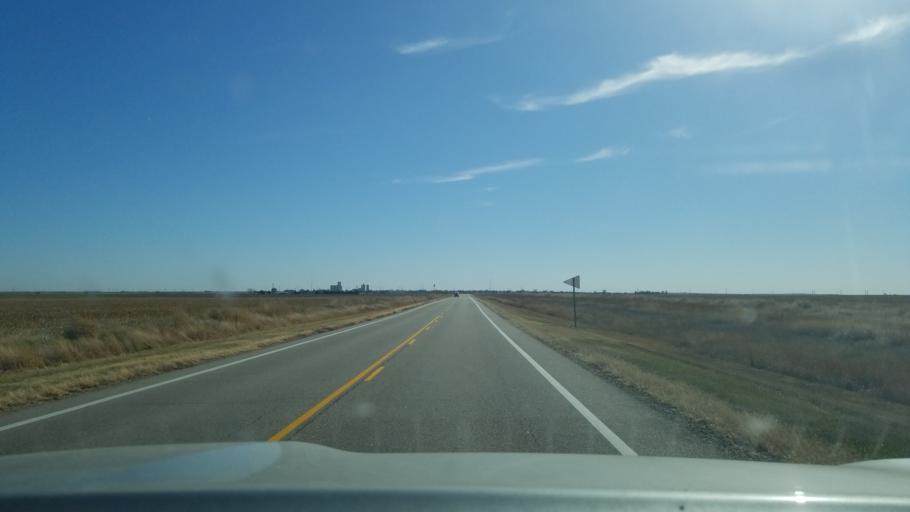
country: US
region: Kansas
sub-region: Kiowa County
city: Greensburg
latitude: 37.5690
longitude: -99.6614
